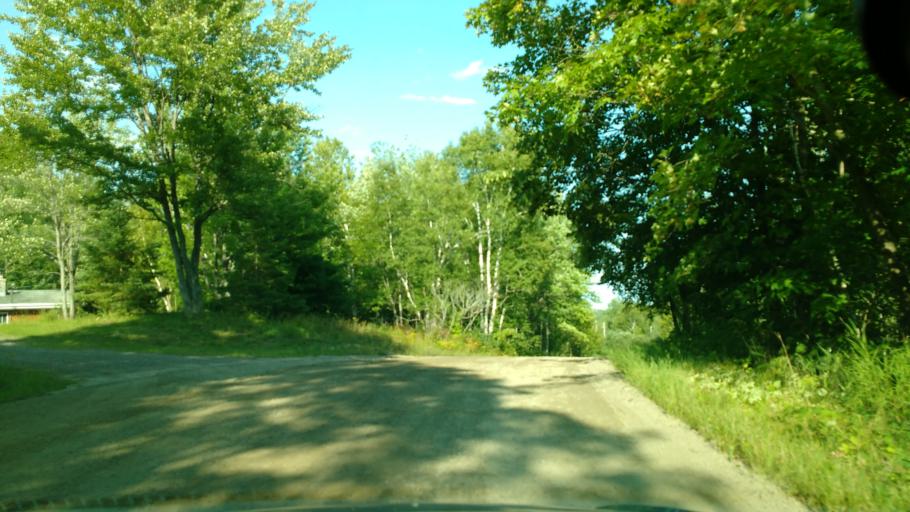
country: CA
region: Ontario
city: Powassan
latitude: 46.1817
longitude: -79.2981
